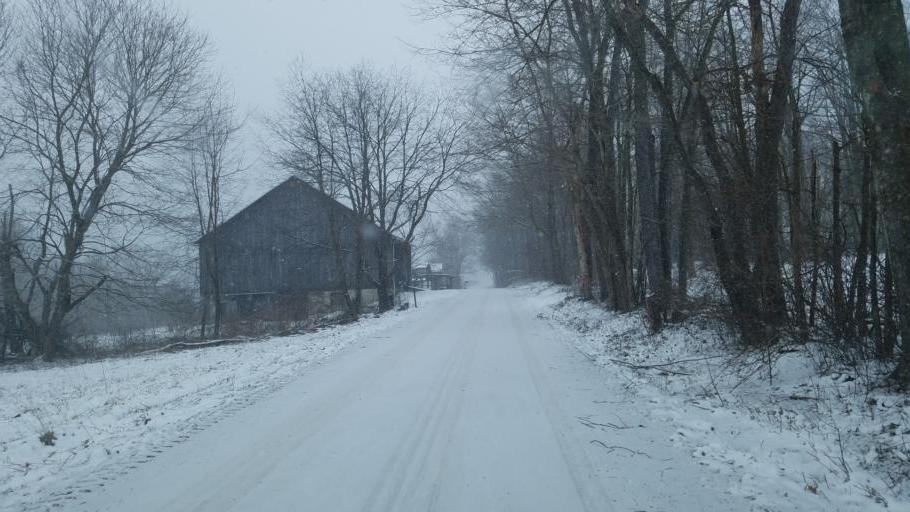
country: US
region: Pennsylvania
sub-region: Venango County
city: Sugarcreek
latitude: 41.4699
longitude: -79.9426
